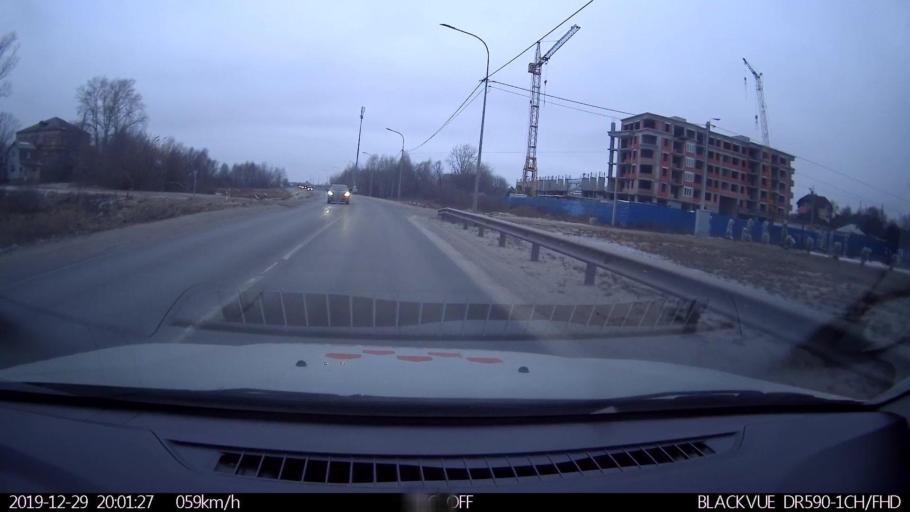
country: RU
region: Nizjnij Novgorod
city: Bor
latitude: 56.3596
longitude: 44.0434
